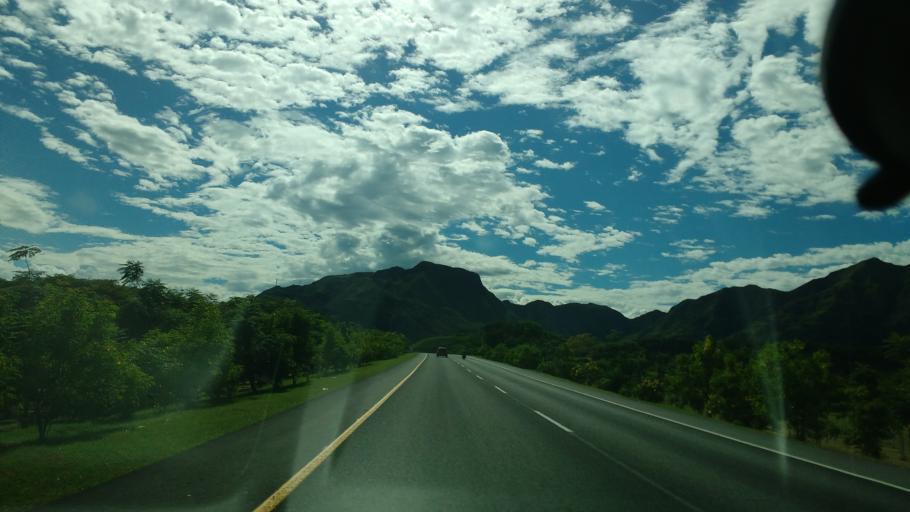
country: CO
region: Tolima
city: Valle de San Juan
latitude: 4.2742
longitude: -75.0027
